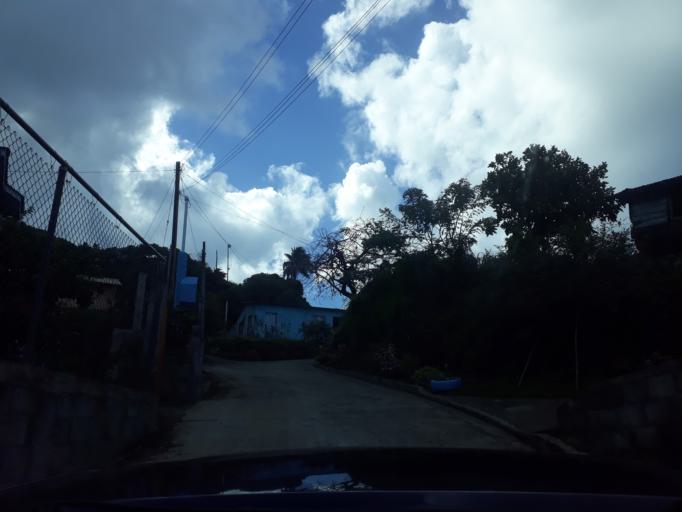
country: VC
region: Charlotte
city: Georgetown
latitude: 13.3806
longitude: -61.1727
